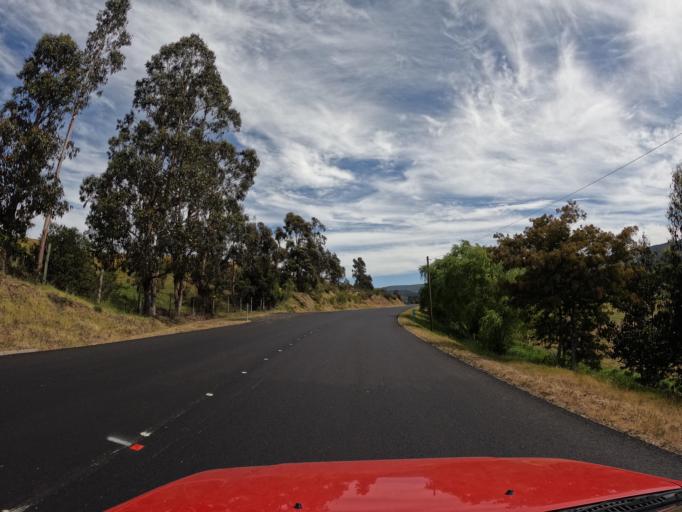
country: CL
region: Maule
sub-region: Provincia de Talca
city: Constitucion
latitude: -35.0716
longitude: -72.0387
